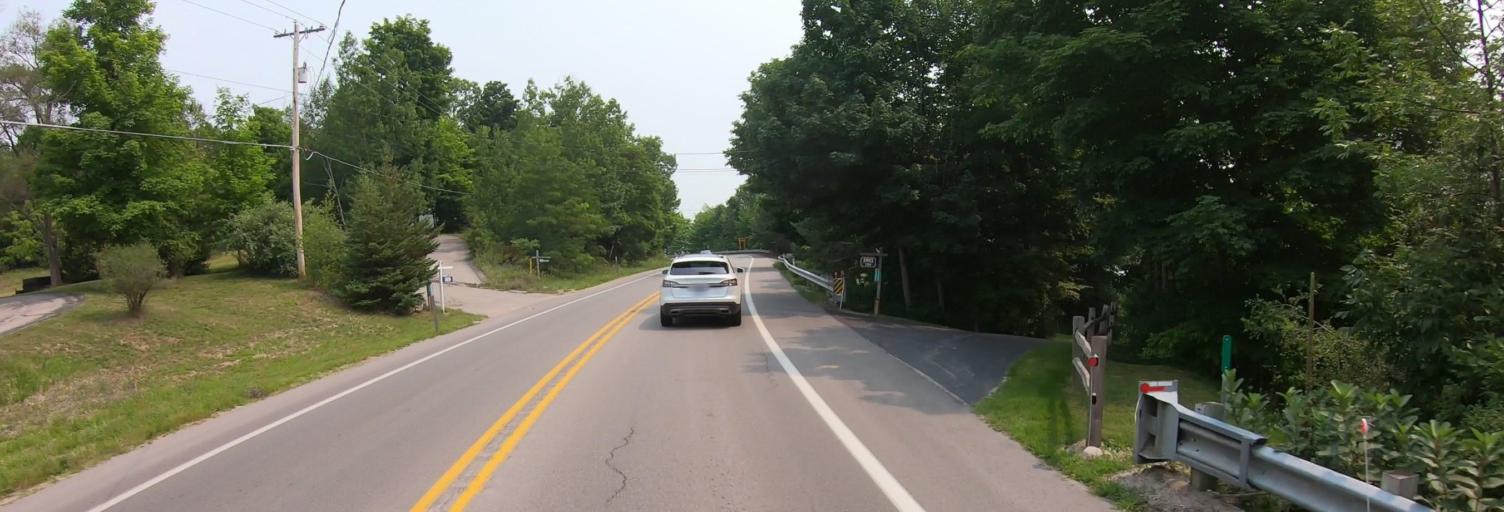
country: US
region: Michigan
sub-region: Leelanau County
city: Leland
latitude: 45.0028
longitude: -85.7705
